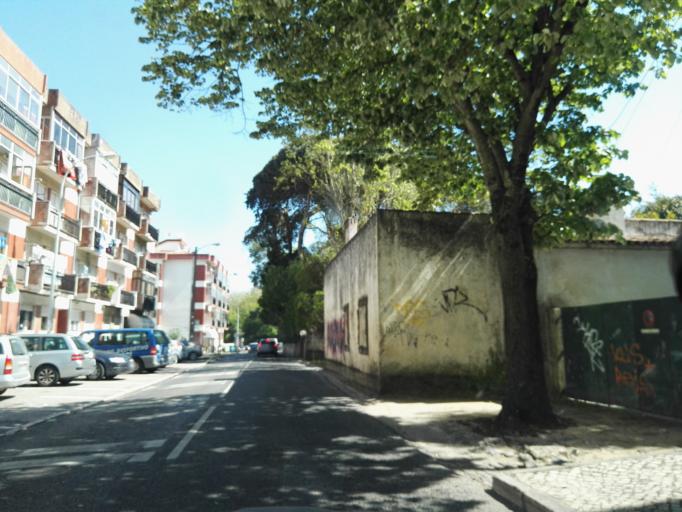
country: PT
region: Lisbon
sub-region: Sintra
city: Rio de Mouro
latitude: 38.7945
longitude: -9.3477
